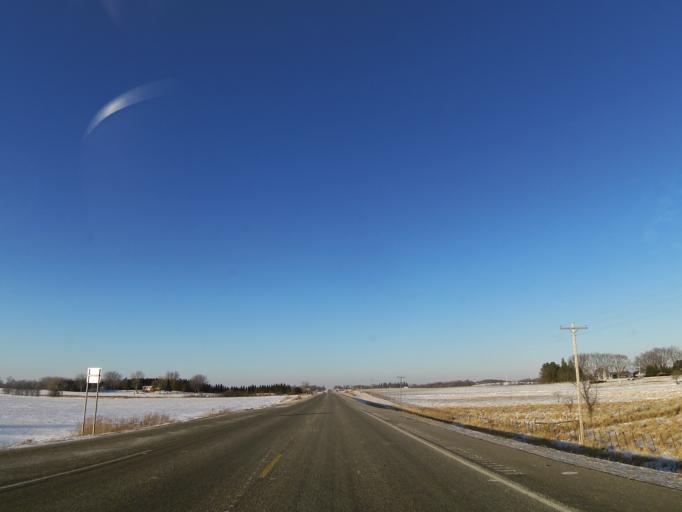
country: US
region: Minnesota
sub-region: Rice County
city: Lonsdale
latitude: 44.5012
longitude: -93.4427
